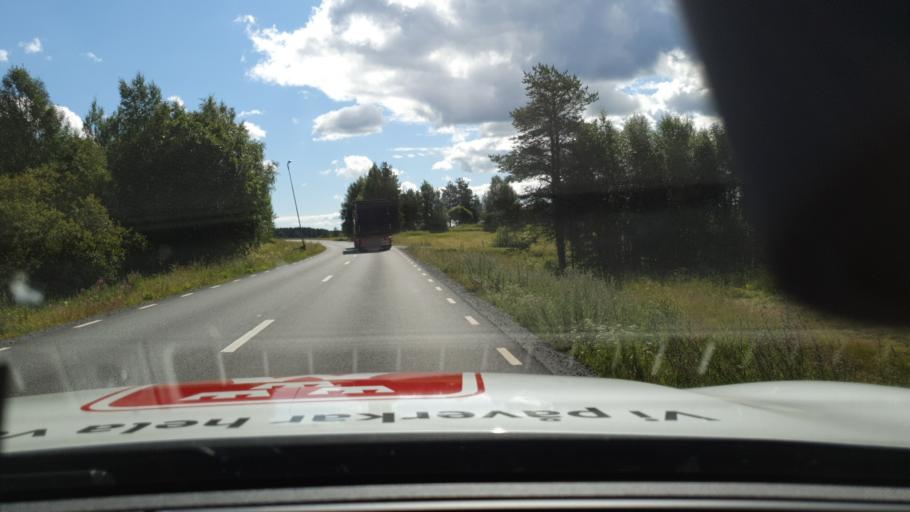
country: SE
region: Norrbotten
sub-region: Lulea Kommun
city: Gammelstad
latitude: 65.8042
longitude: 22.0353
